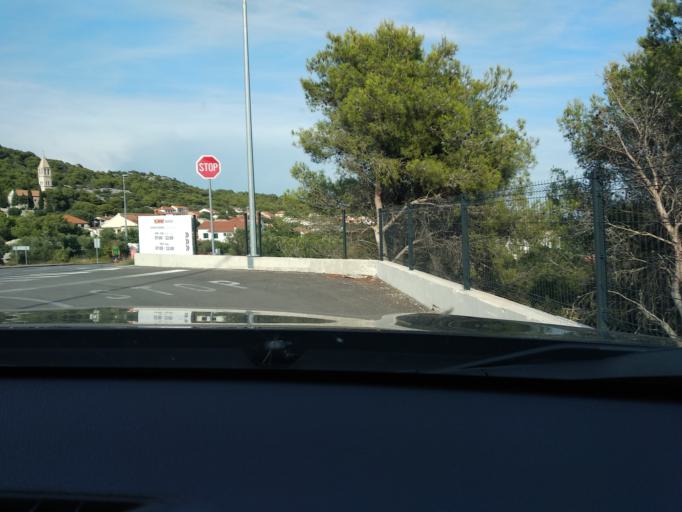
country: HR
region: Sibensko-Kniniska
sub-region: Grad Sibenik
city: Tisno
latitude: 43.7894
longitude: 15.6319
